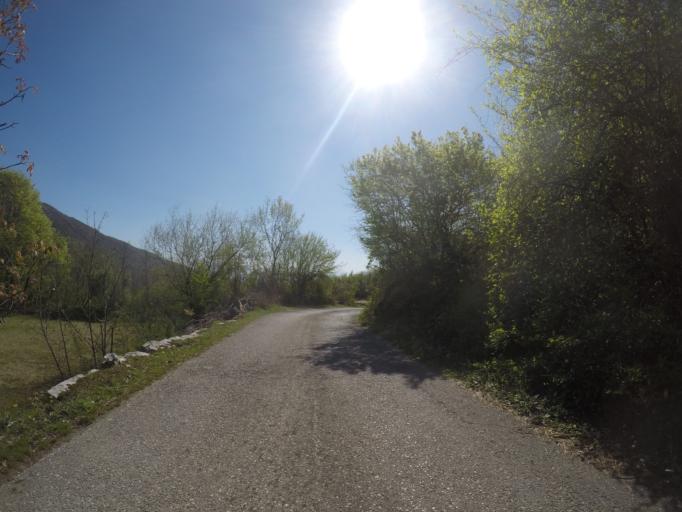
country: ME
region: Danilovgrad
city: Danilovgrad
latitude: 42.5158
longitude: 19.0541
